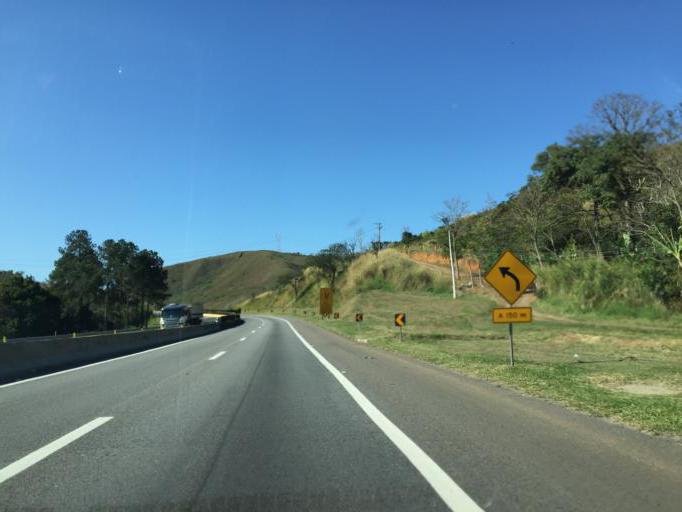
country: BR
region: Sao Paulo
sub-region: Cruzeiro
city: Cruzeiro
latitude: -22.6475
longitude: -44.9535
